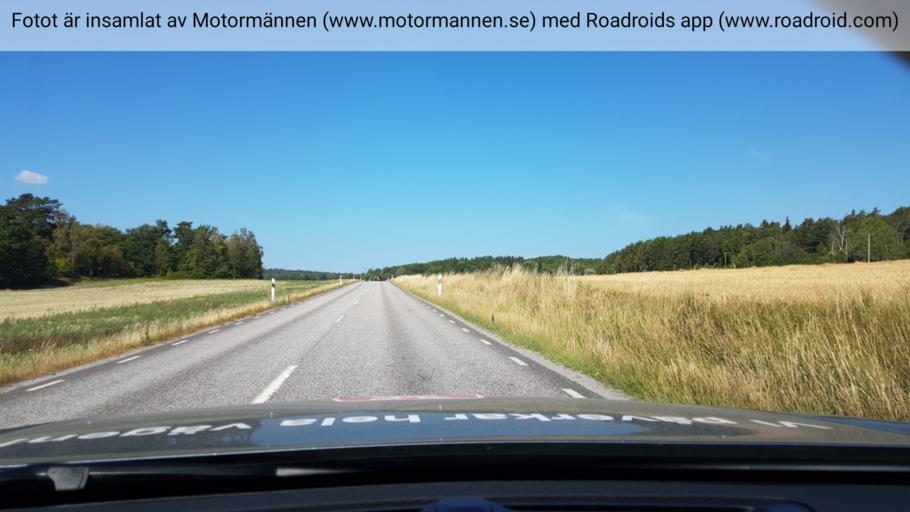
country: SE
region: Stockholm
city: Stenhamra
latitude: 59.2942
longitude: 17.6807
